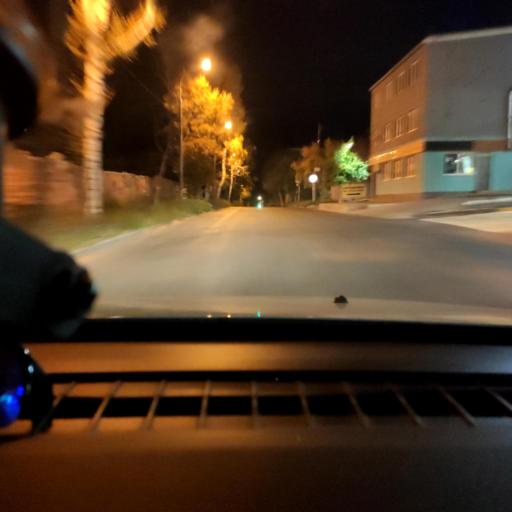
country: RU
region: Samara
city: Rozhdestveno
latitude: 53.1768
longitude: 50.0793
